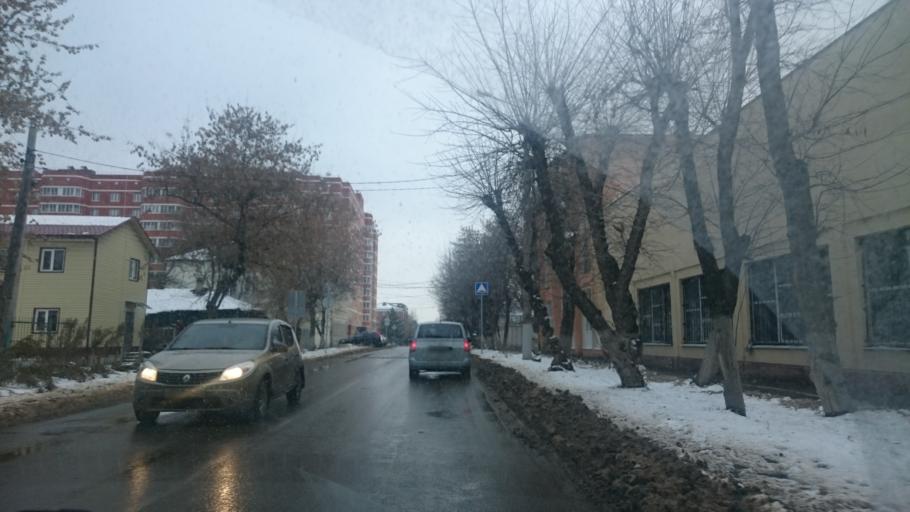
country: RU
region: Tula
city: Tula
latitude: 54.2090
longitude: 37.6163
